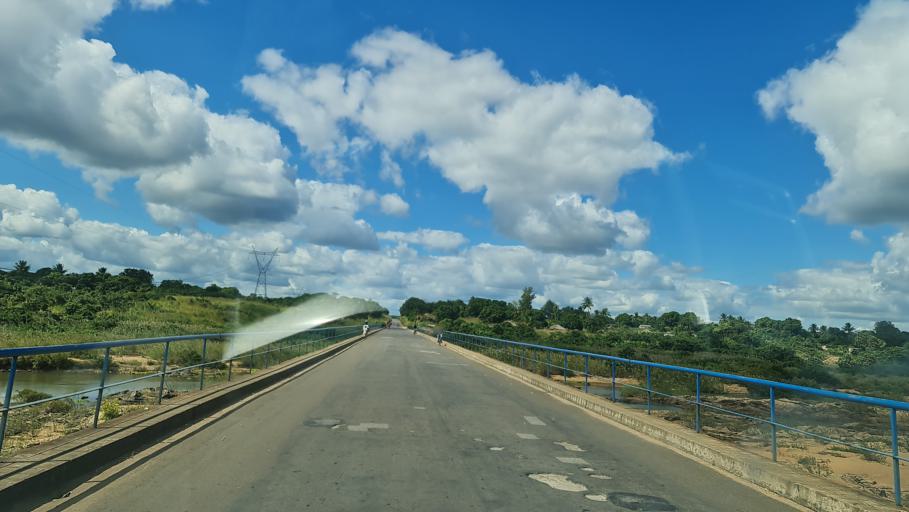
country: MZ
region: Zambezia
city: Quelimane
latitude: -17.5251
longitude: 36.2721
